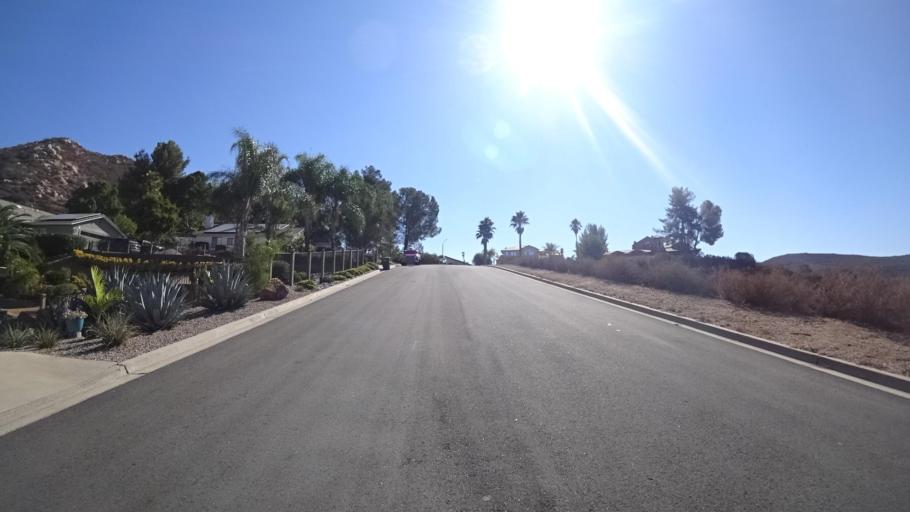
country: US
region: California
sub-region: San Diego County
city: San Diego Country Estates
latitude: 33.0041
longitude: -116.7671
